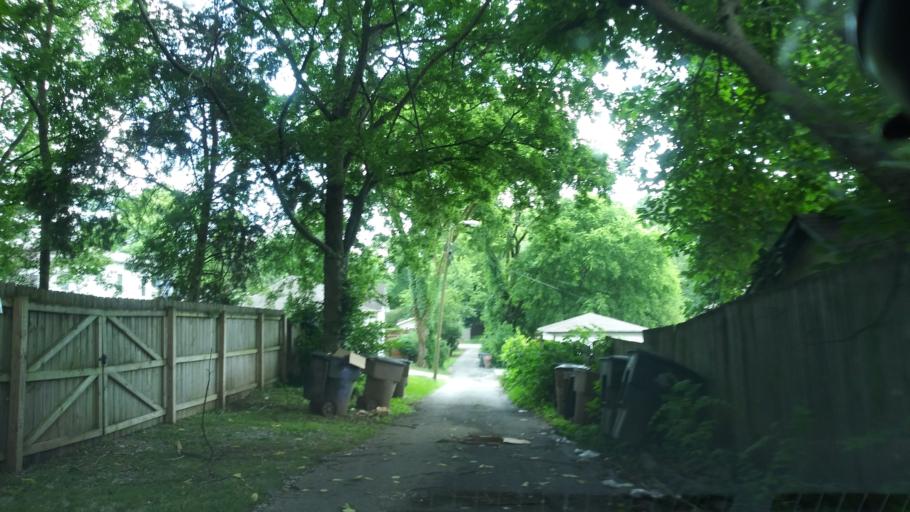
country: US
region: Tennessee
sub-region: Davidson County
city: Belle Meade
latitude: 36.1507
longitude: -86.8478
